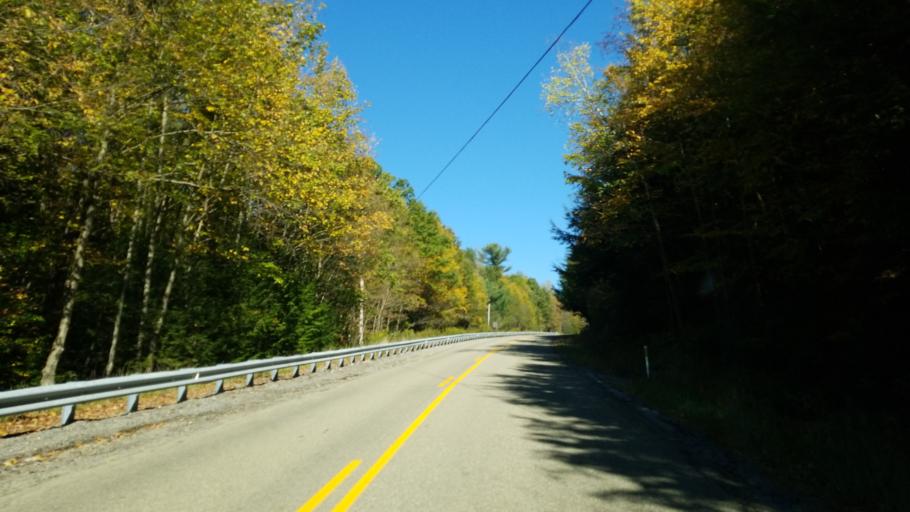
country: US
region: Pennsylvania
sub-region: Clearfield County
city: Shiloh
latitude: 41.2527
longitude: -78.3705
